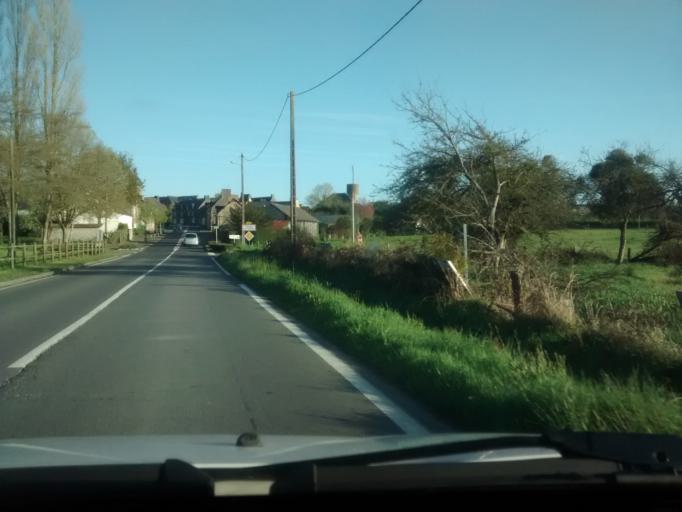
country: FR
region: Brittany
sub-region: Departement d'Ille-et-Vilaine
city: Pleine-Fougeres
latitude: 48.4948
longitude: -1.5855
